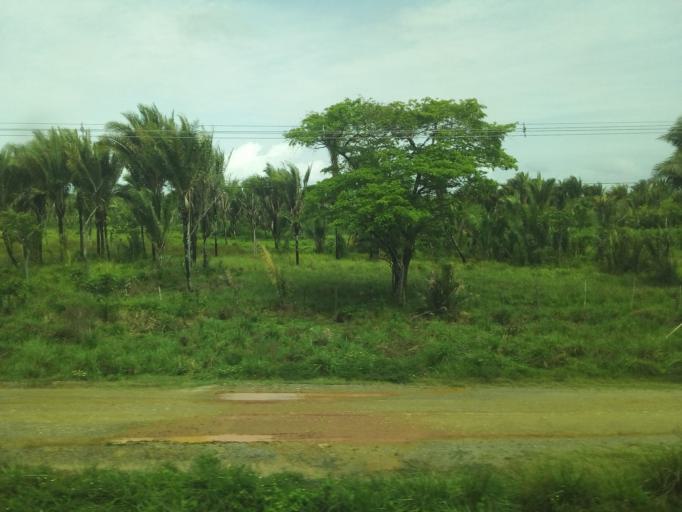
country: BR
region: Maranhao
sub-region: Anajatuba
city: Anajatuba
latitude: -3.4068
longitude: -44.5423
